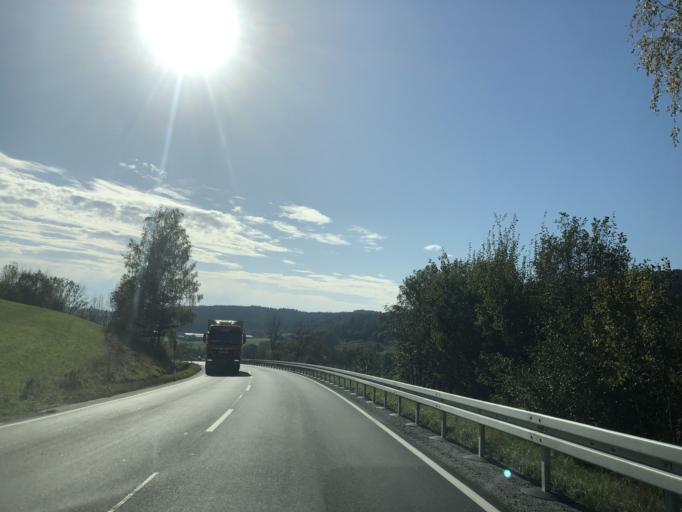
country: DE
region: Bavaria
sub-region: Lower Bavaria
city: Grafling
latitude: 48.8864
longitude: 12.9676
